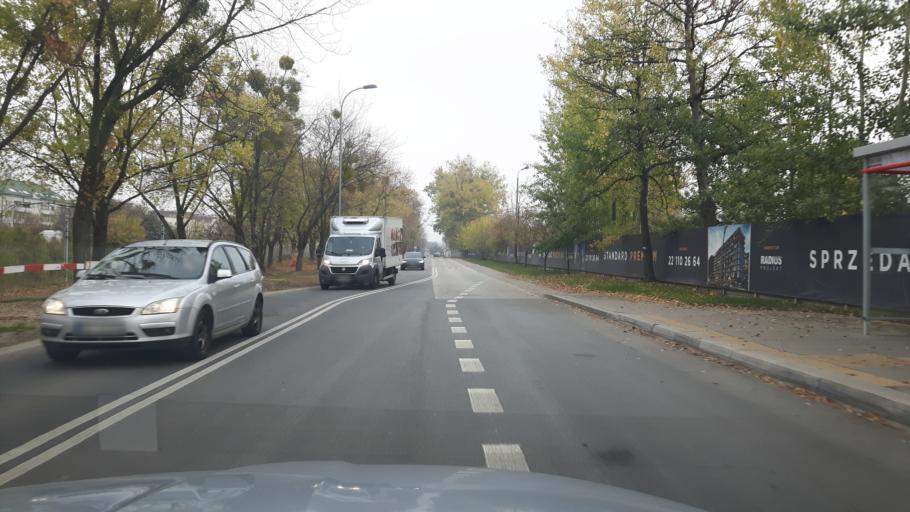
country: PL
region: Masovian Voivodeship
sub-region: Warszawa
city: Wlochy
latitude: 52.1991
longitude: 20.9545
